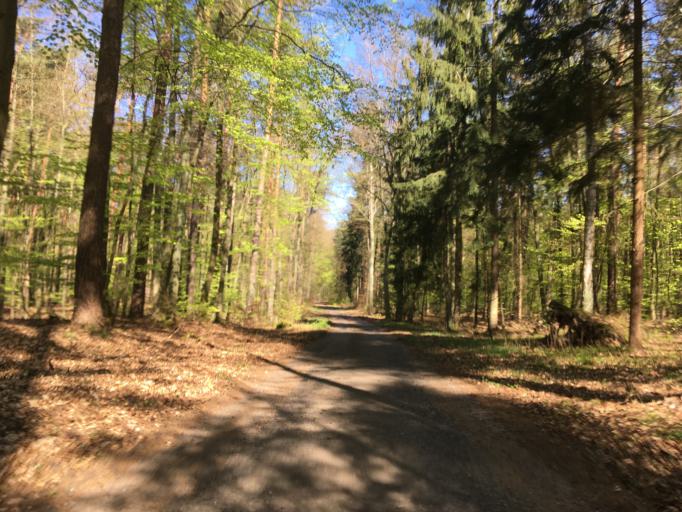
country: DE
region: Brandenburg
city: Wandlitz
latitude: 52.7504
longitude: 13.5365
